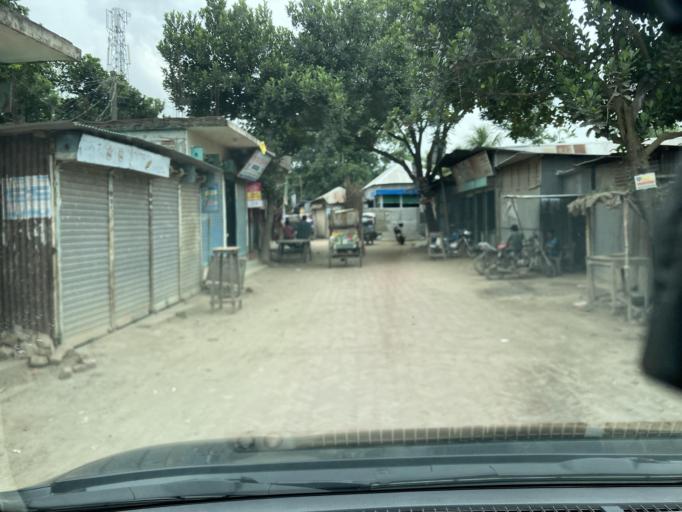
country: BD
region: Dhaka
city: Dohar
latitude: 23.7813
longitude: 90.0664
